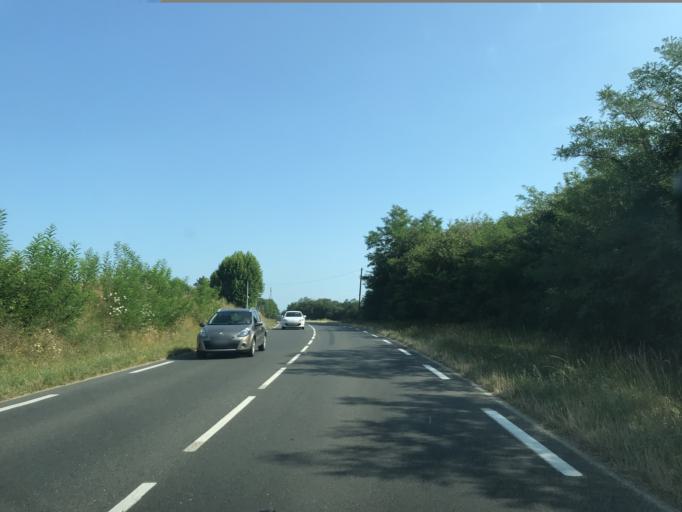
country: FR
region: Aquitaine
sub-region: Departement de la Dordogne
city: Sarlat-la-Caneda
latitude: 44.9484
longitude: 1.2232
